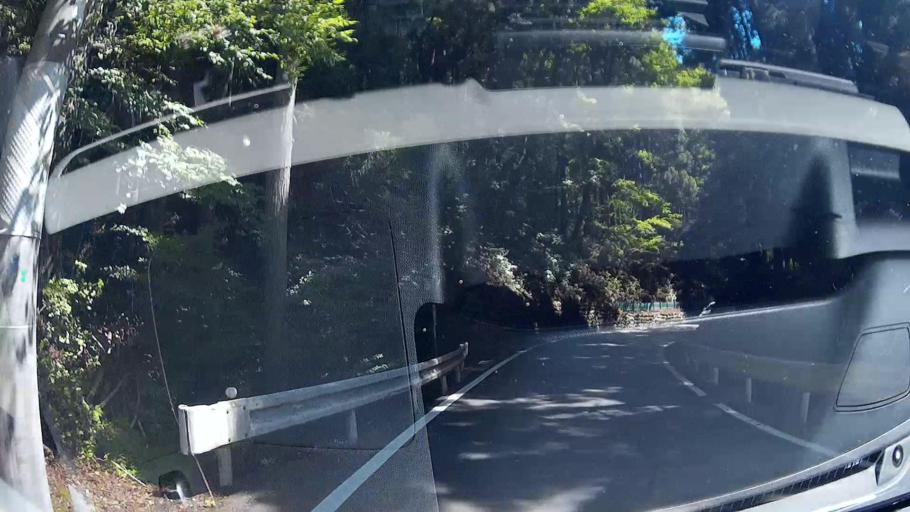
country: JP
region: Shizuoka
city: Shizuoka-shi
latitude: 35.2023
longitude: 138.2499
